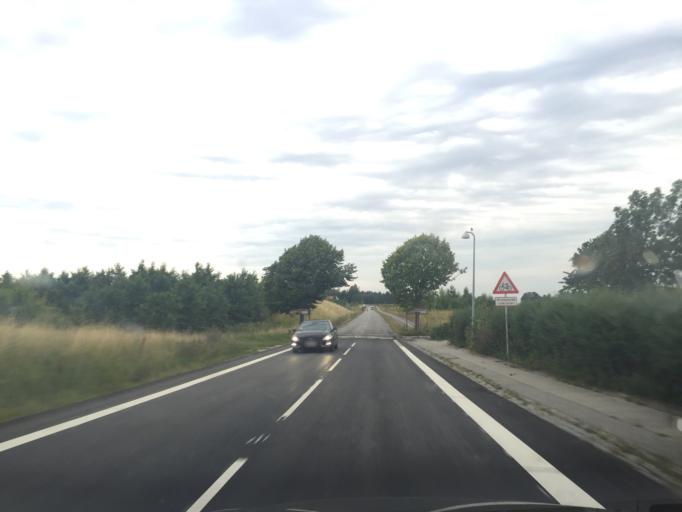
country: DK
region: Zealand
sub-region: Roskilde Kommune
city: Gundsomagle
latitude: 55.7403
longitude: 12.1477
